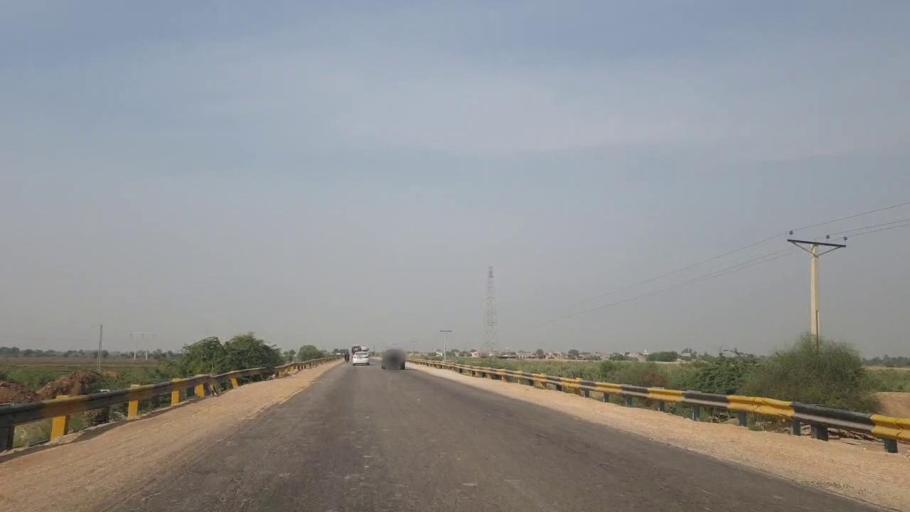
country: PK
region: Sindh
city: Sann
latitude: 26.0822
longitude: 68.0938
